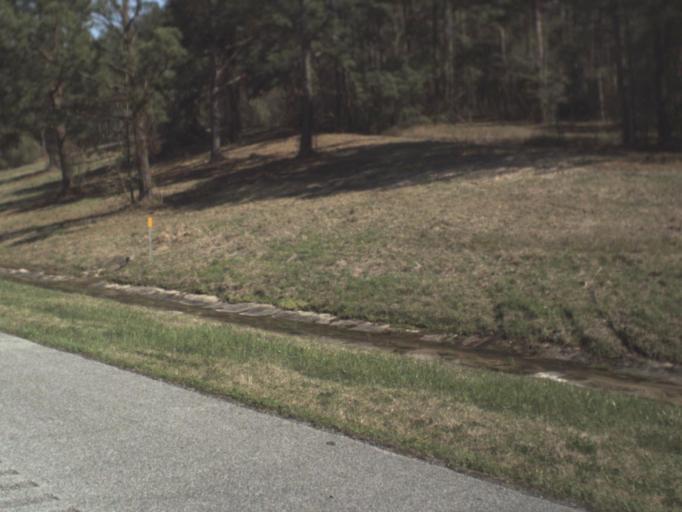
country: US
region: Florida
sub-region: Jackson County
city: Sneads
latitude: 30.6385
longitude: -84.9254
